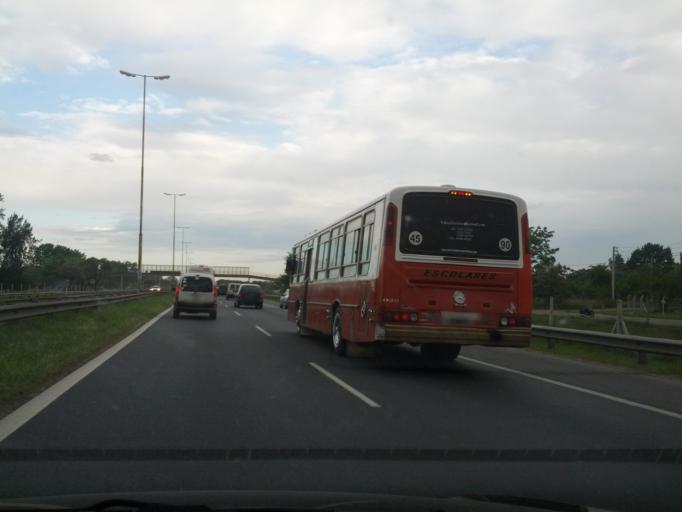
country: AR
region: Buenos Aires
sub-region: Partido de General Rodriguez
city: General Rodriguez
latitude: -34.6007
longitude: -58.9121
